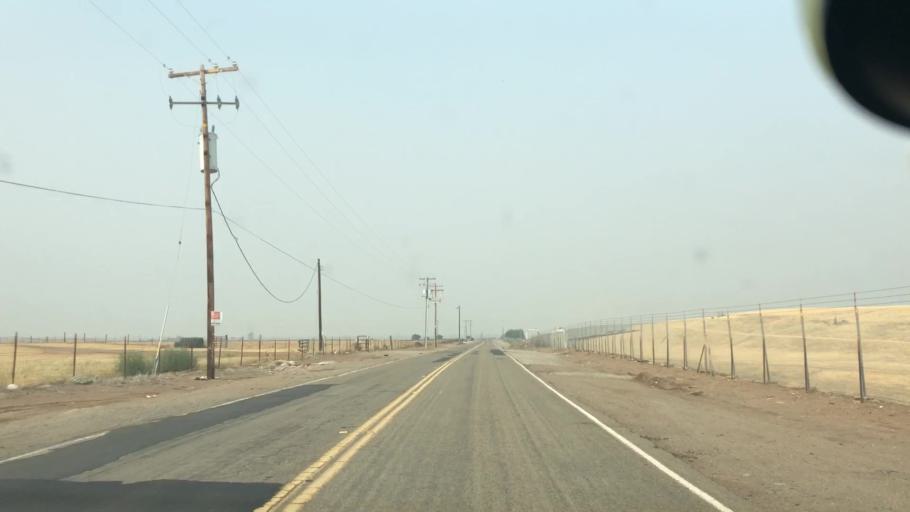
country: US
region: California
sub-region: San Joaquin County
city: Tracy
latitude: 37.6683
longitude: -121.4623
